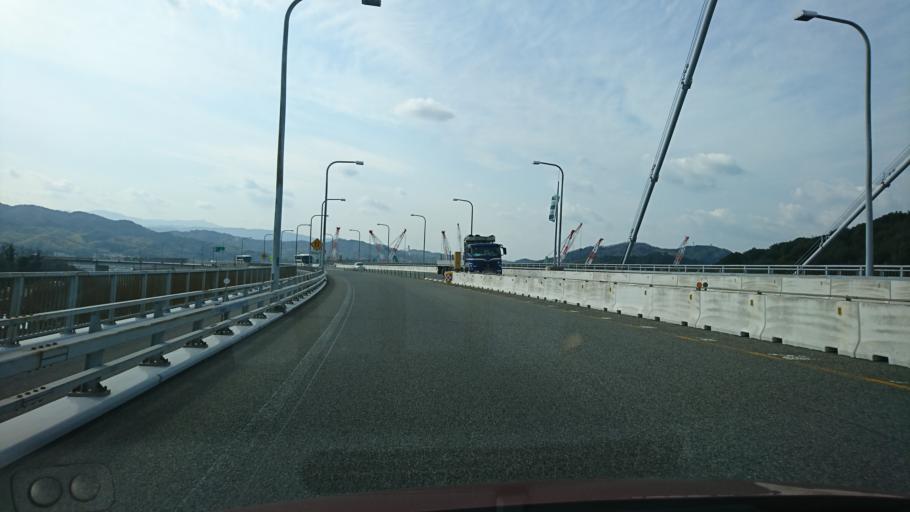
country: JP
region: Hiroshima
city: Takehara
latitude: 34.1126
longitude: 132.9783
